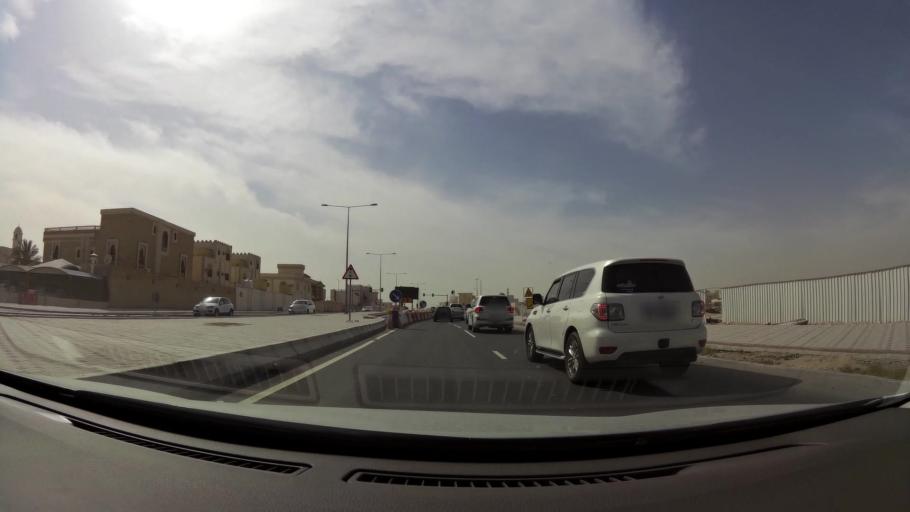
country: QA
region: Baladiyat ar Rayyan
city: Ar Rayyan
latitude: 25.3224
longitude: 51.3963
